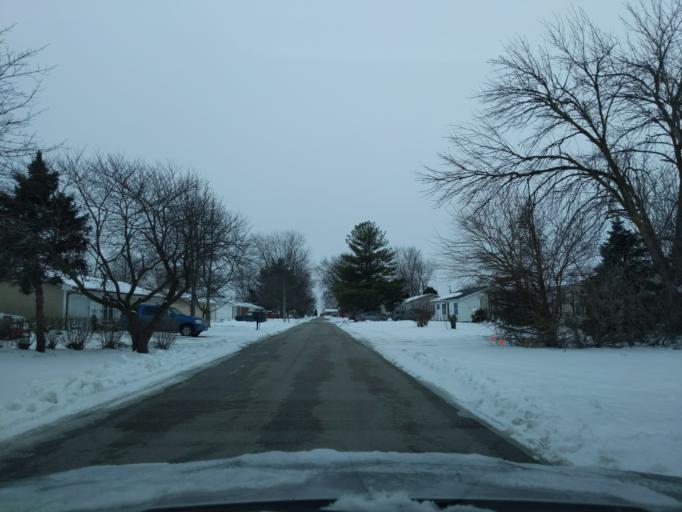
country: US
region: Indiana
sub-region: Benton County
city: Otterbein
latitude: 40.4844
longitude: -87.0918
